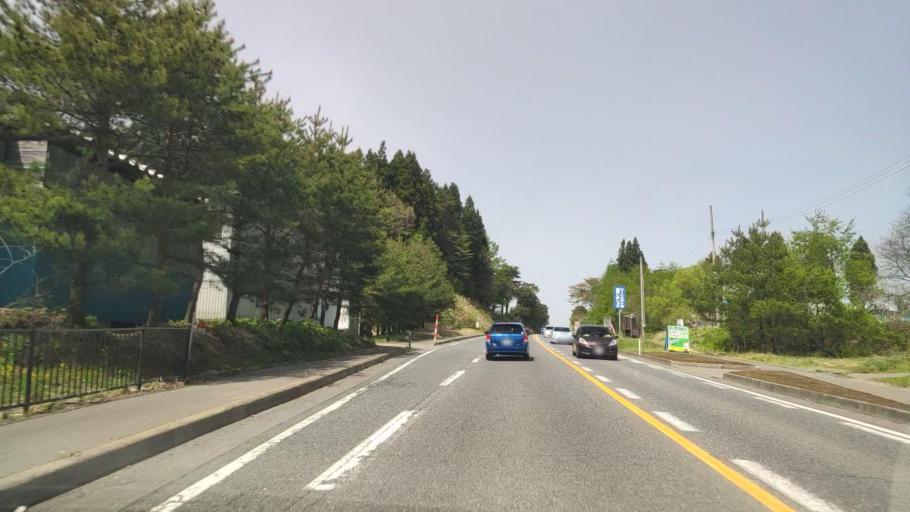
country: JP
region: Aomori
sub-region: Misawa Shi
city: Inuotose
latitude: 40.6657
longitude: 141.1863
